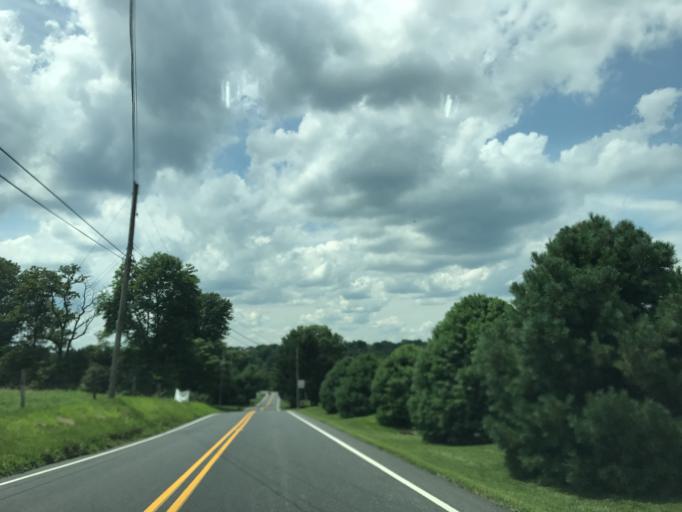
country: US
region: Pennsylvania
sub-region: Lancaster County
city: Mount Joy
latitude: 40.1815
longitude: -76.4862
